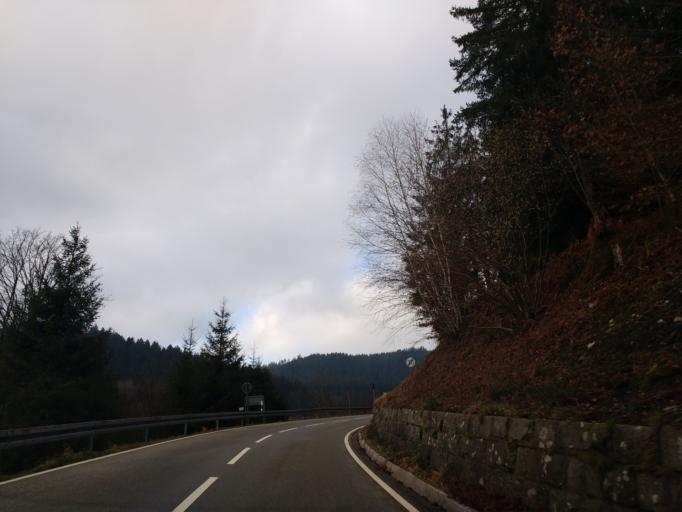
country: DE
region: Baden-Wuerttemberg
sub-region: Karlsruhe Region
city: Bad Rippoldsau-Schapbach
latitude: 48.4488
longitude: 8.2934
